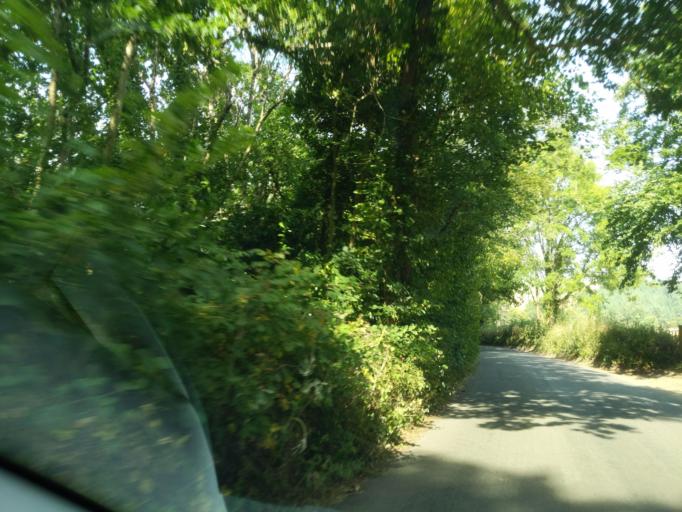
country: GB
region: England
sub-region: Devon
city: Winkleigh
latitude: 50.8842
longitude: -3.8799
